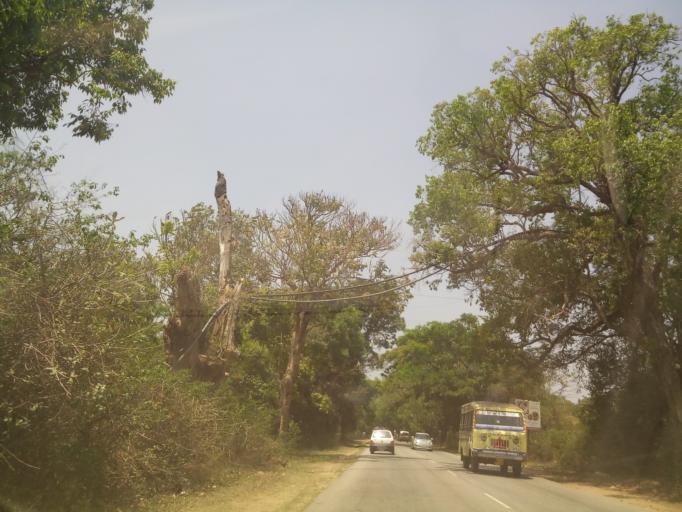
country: IN
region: Karnataka
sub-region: Hassan
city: Alur
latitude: 12.9480
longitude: 75.9468
